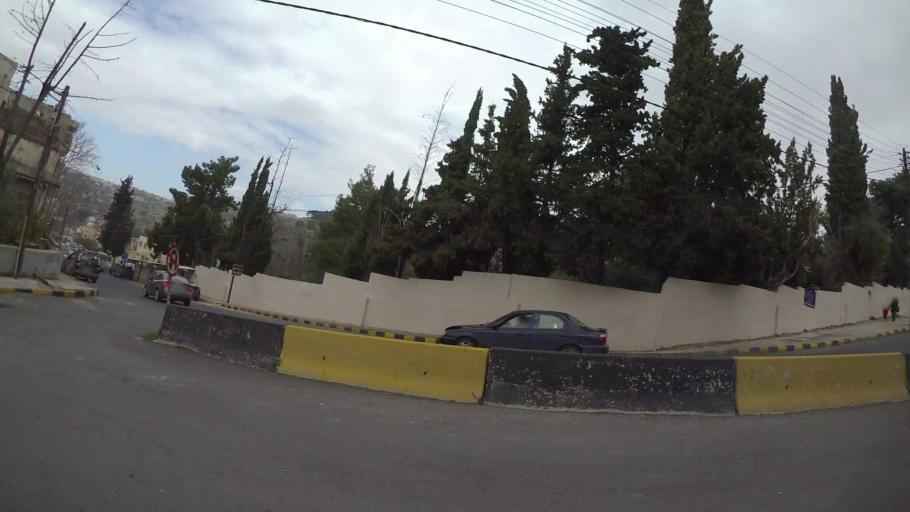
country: JO
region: Amman
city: Wadi as Sir
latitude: 31.9522
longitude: 35.8207
